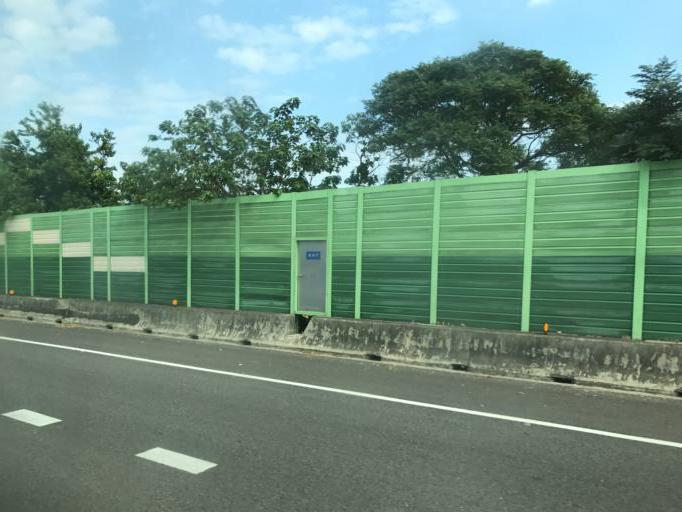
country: TW
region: Taiwan
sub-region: Hsinchu
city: Zhubei
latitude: 24.8047
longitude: 121.0098
